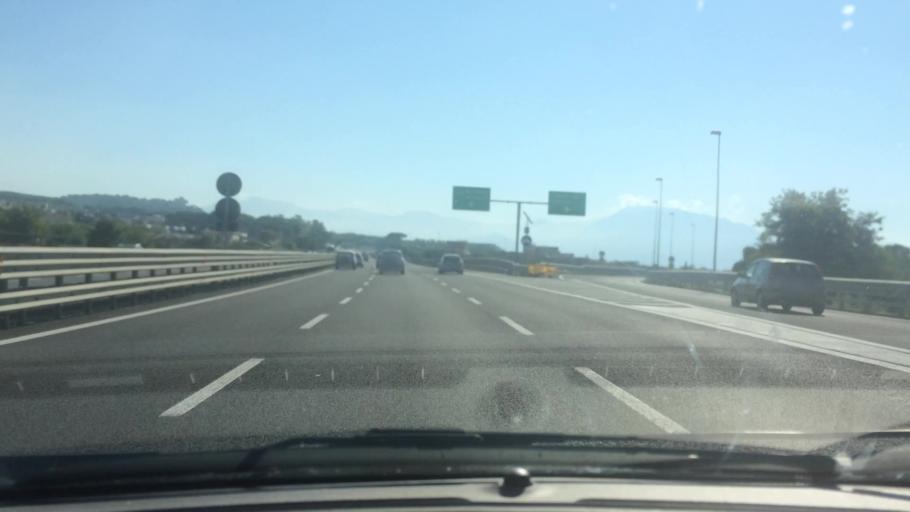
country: IT
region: Campania
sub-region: Provincia di Napoli
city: Torre del Greco
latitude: 40.7897
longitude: 14.3794
